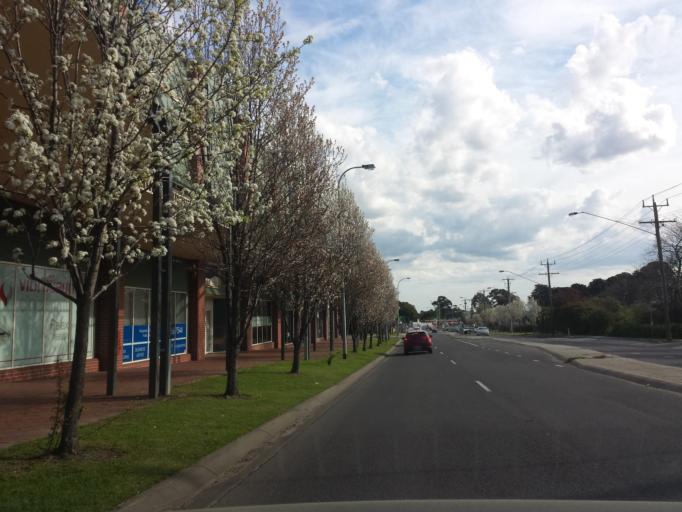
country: AU
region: Victoria
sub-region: Casey
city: Berwick
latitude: -38.0291
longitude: 145.3468
